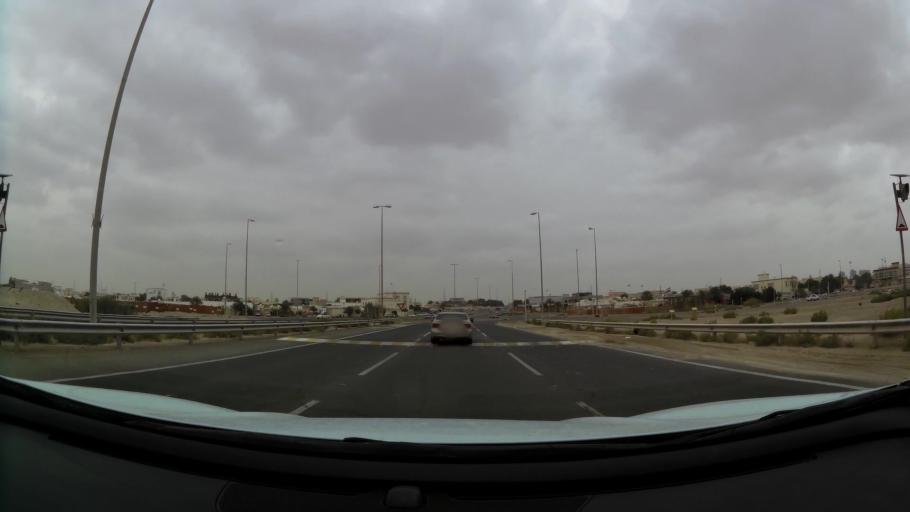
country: AE
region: Abu Dhabi
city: Abu Dhabi
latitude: 24.3273
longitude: 54.6370
